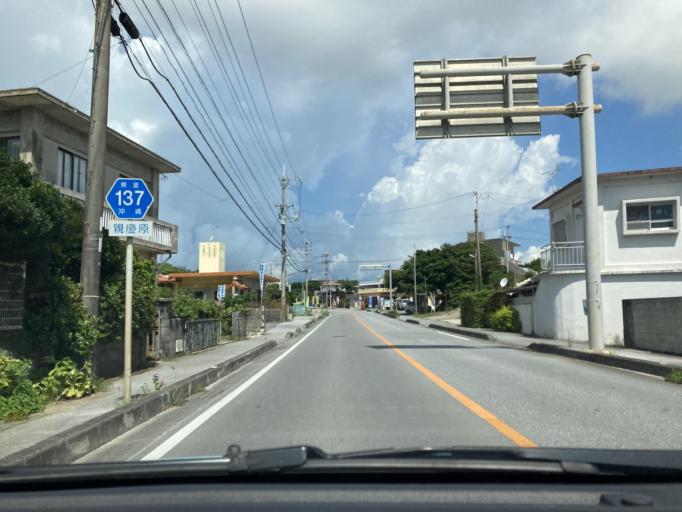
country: JP
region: Okinawa
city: Tomigusuku
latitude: 26.1560
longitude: 127.7804
